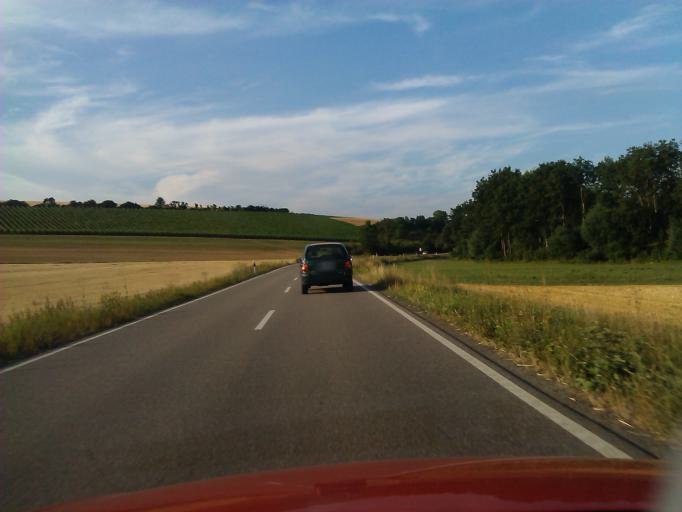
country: DE
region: Baden-Wuerttemberg
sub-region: Regierungsbezirk Stuttgart
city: Gemmingen
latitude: 49.1191
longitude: 8.9948
